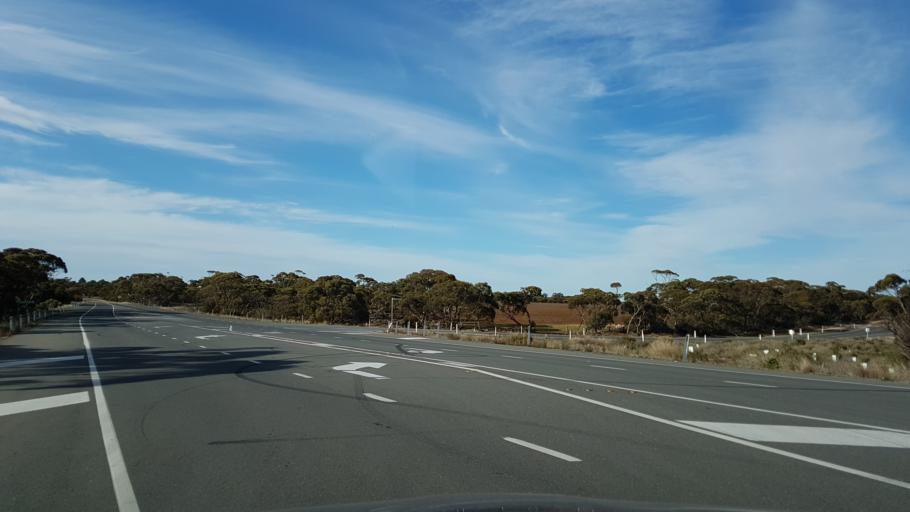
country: AU
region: South Australia
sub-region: Murray Bridge
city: Tailem Bend
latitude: -35.0874
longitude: 139.4652
